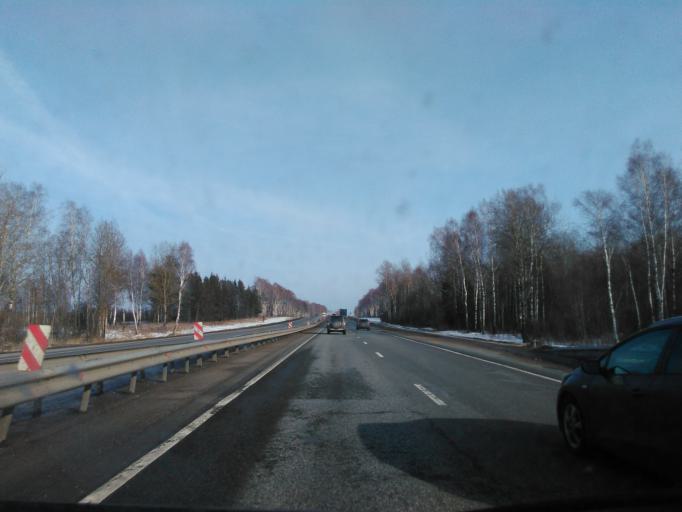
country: RU
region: Smolensk
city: Verkhnedneprovskiy
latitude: 55.1814
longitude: 33.5898
